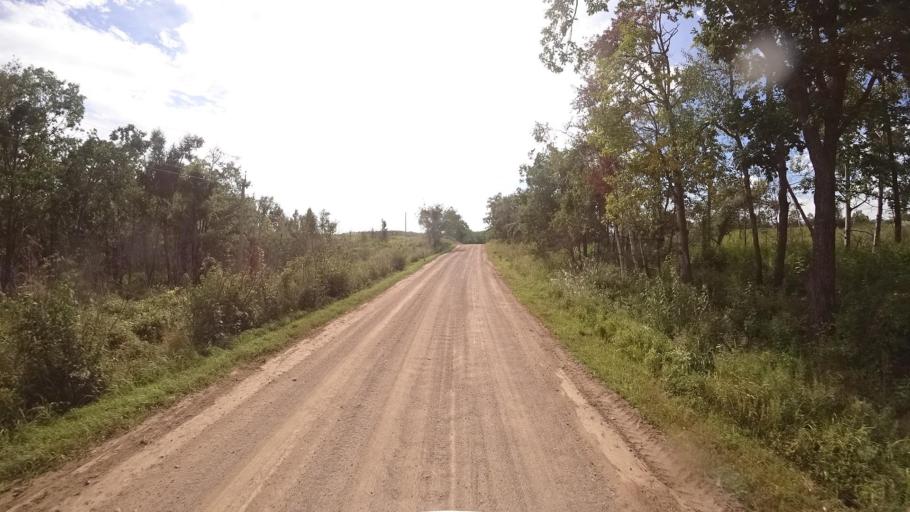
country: RU
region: Primorskiy
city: Dostoyevka
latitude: 44.3422
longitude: 133.5092
